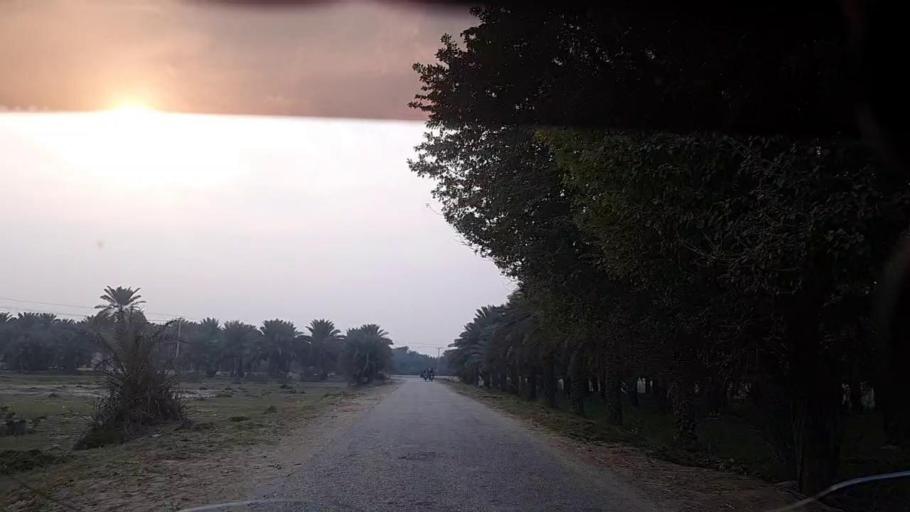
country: PK
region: Sindh
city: Khairpur
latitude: 27.5019
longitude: 68.6881
